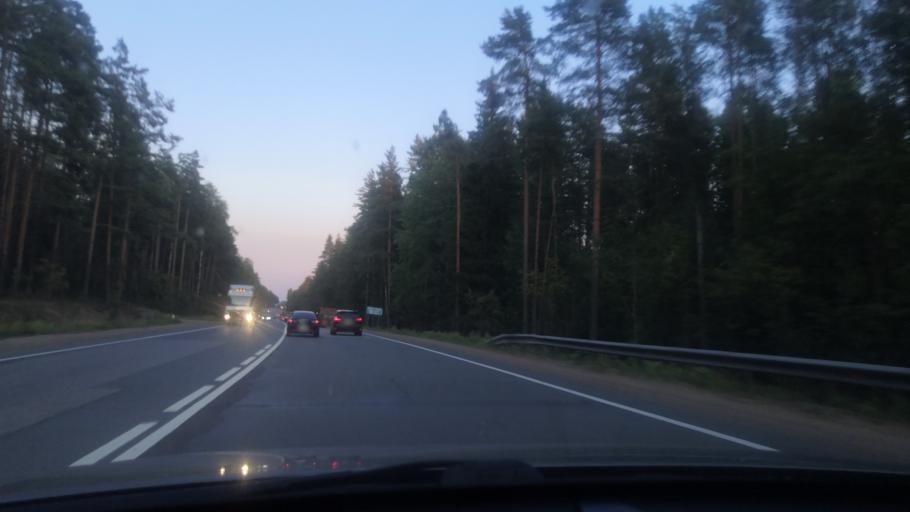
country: RU
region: St.-Petersburg
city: Solnechnoye
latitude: 60.2035
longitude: 29.9560
